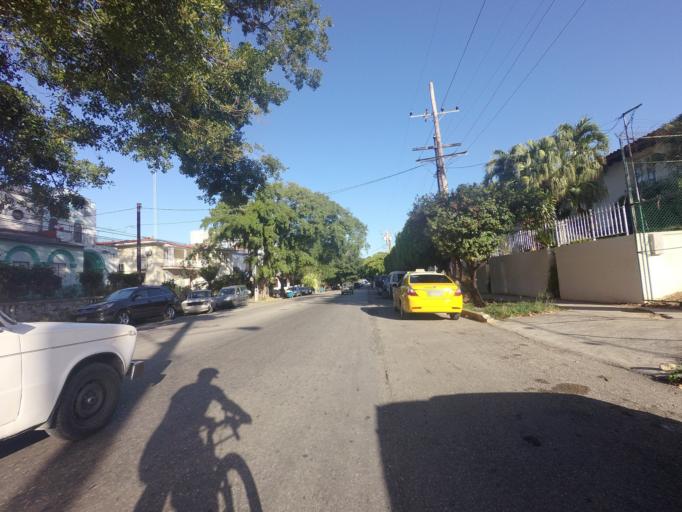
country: CU
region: La Habana
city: Havana
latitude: 23.1182
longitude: -82.4236
